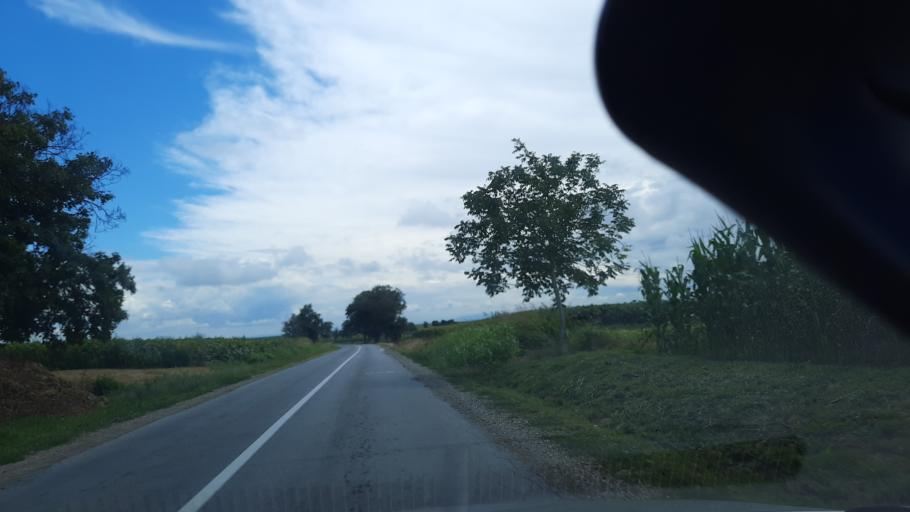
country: RS
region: Autonomna Pokrajina Vojvodina
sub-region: Sremski Okrug
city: Sremska Mitrovica
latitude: 45.1060
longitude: 19.5675
